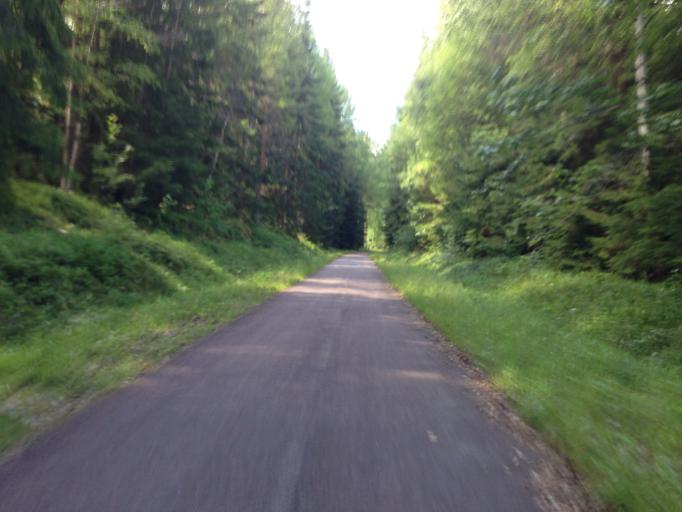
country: SE
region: Dalarna
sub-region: Ludvika Kommun
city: Grangesberg
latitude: 60.2081
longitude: 15.0538
